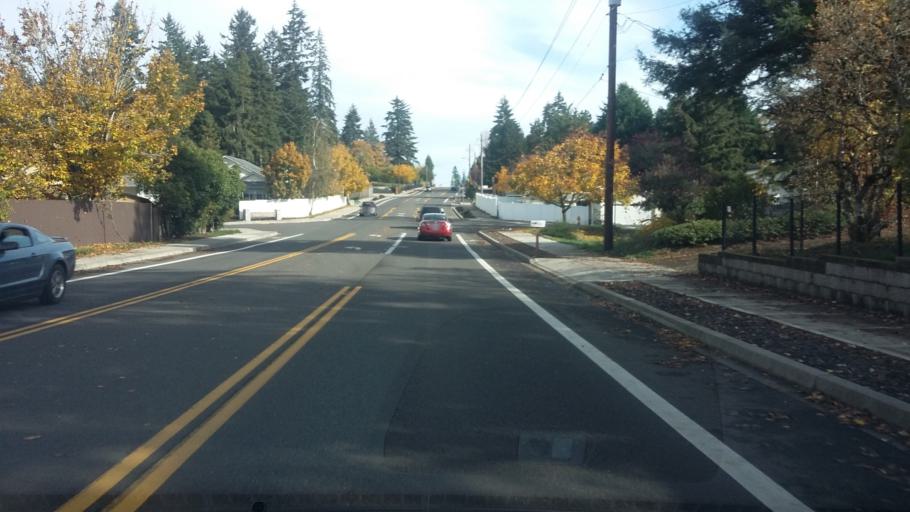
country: US
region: Washington
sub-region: Clark County
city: Hazel Dell
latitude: 45.6860
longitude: -122.6429
